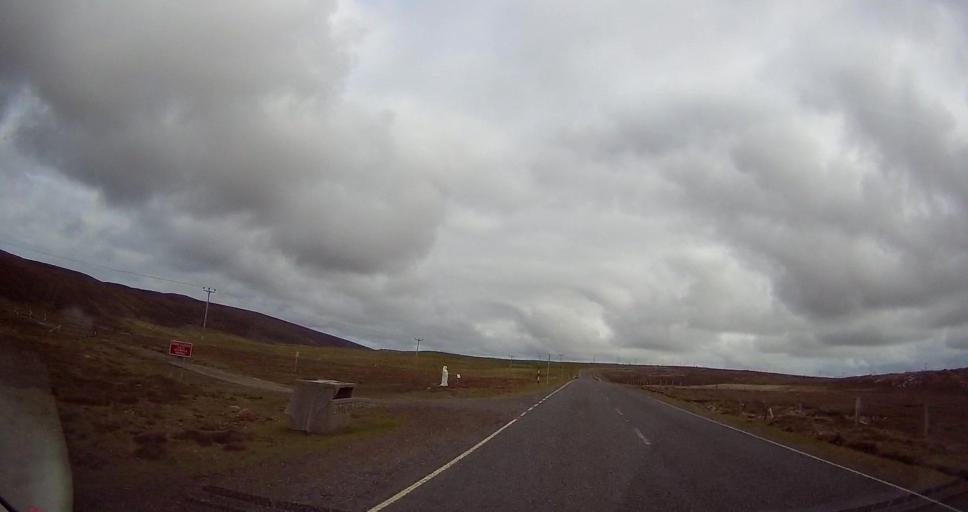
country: GB
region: Scotland
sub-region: Shetland Islands
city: Shetland
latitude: 60.7196
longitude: -0.9112
